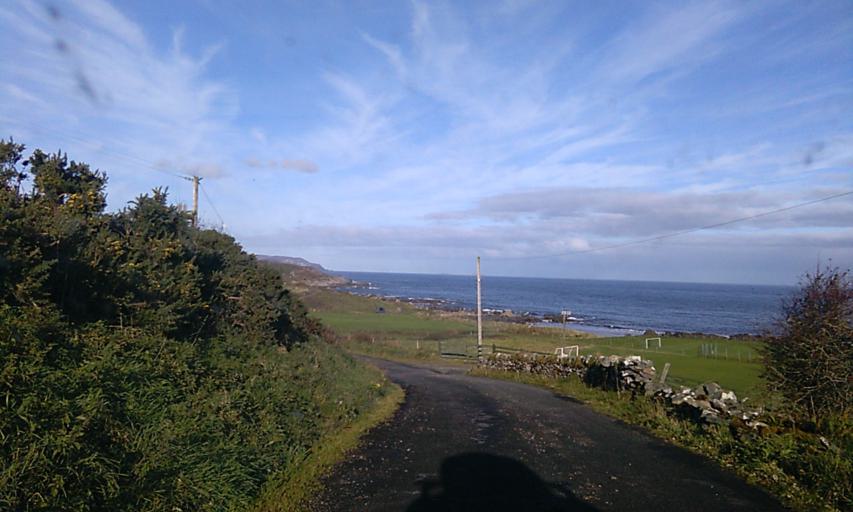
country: IE
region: Ulster
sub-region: County Donegal
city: Moville
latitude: 55.2697
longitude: -7.0680
